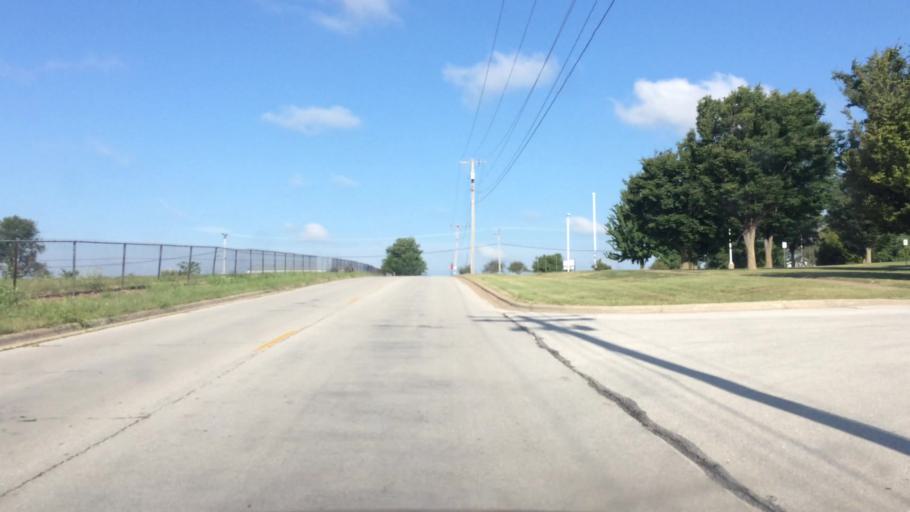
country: US
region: Missouri
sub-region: Greene County
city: Springfield
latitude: 37.2662
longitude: -93.2796
